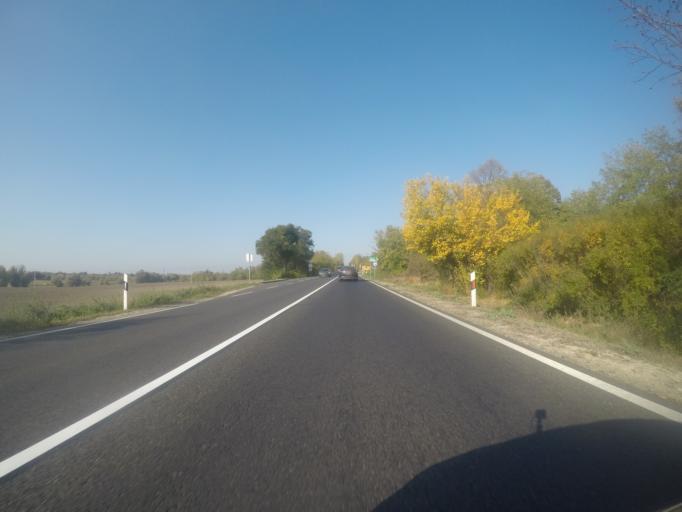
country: HU
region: Fejer
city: Baracs
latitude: 46.8727
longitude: 18.9189
